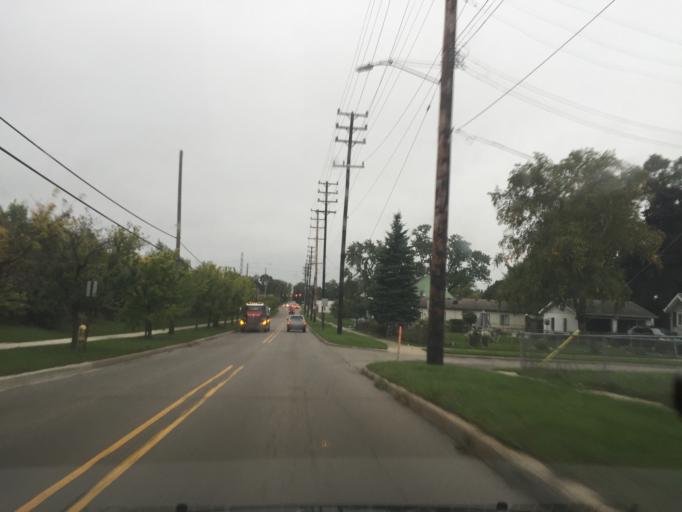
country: US
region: Michigan
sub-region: Oakland County
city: Pontiac
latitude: 42.6221
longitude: -83.2883
